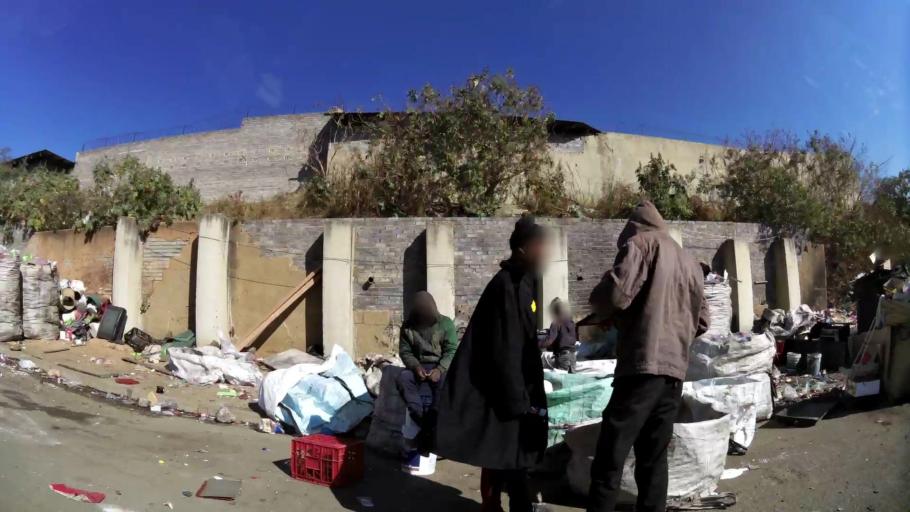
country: ZA
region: Gauteng
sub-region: City of Johannesburg Metropolitan Municipality
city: Modderfontein
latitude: -26.1130
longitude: 28.1079
